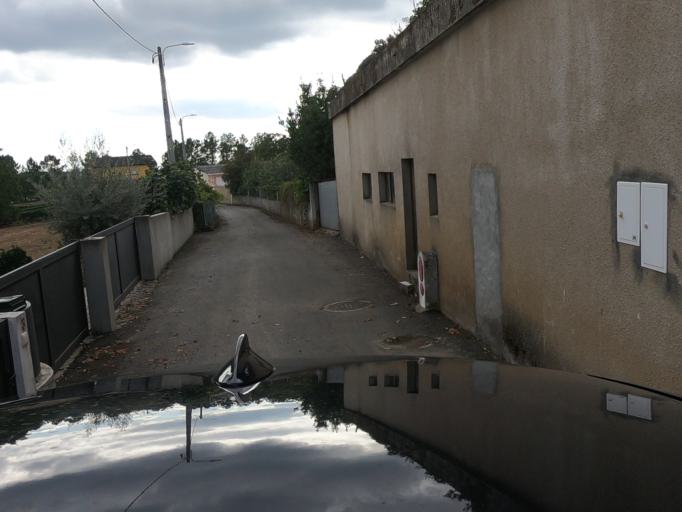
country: PT
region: Vila Real
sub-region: Vila Real
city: Vila Real
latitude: 41.2794
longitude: -7.7027
